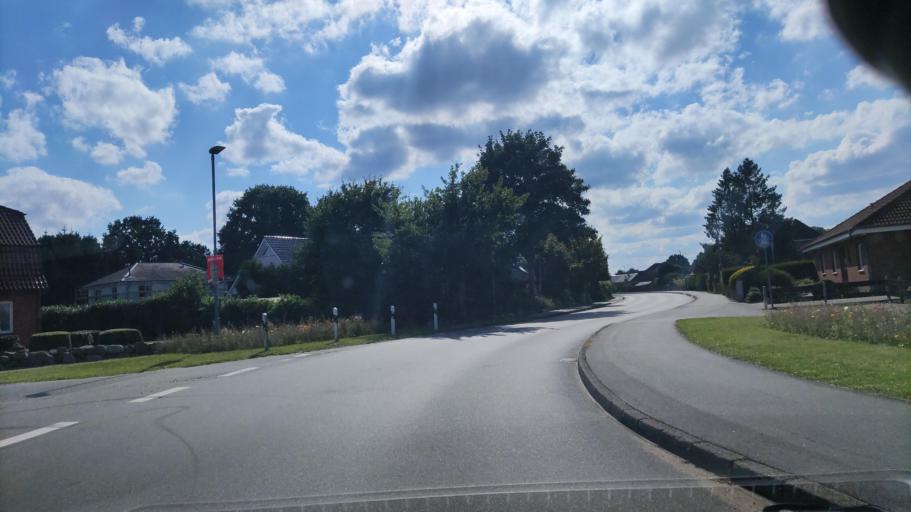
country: DE
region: Schleswig-Holstein
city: Alt Duvenstedt
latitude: 54.3577
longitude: 9.6425
